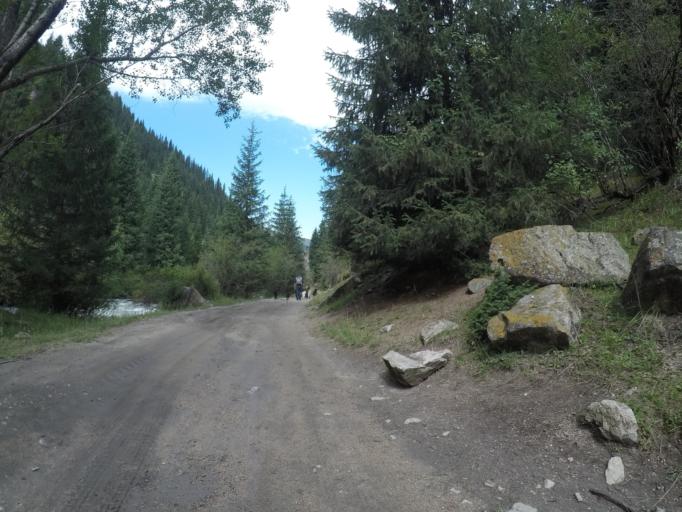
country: KG
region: Ysyk-Koel
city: Teploklyuchenka
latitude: 42.4430
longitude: 78.5520
